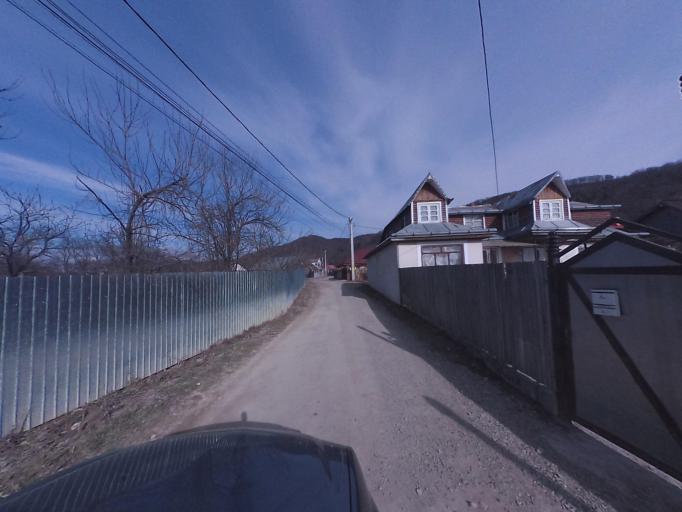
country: RO
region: Neamt
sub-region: Oras Targu Neamt
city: Humulesti
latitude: 47.2128
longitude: 26.3355
